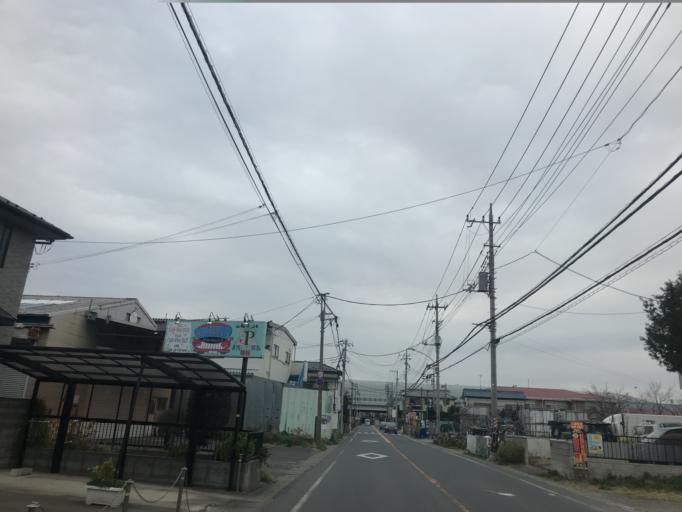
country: JP
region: Saitama
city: Yashio-shi
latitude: 35.8424
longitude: 139.8413
